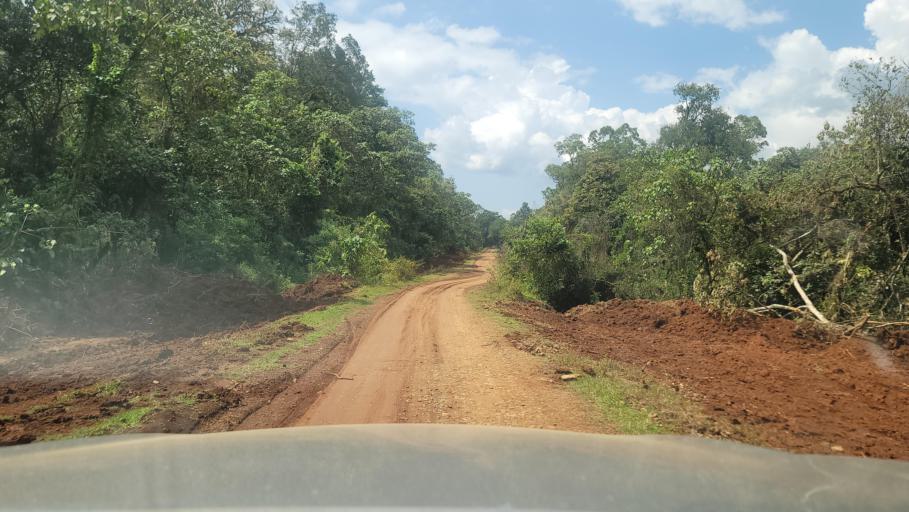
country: ET
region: Southern Nations, Nationalities, and People's Region
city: Bonga
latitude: 7.6435
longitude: 36.2416
